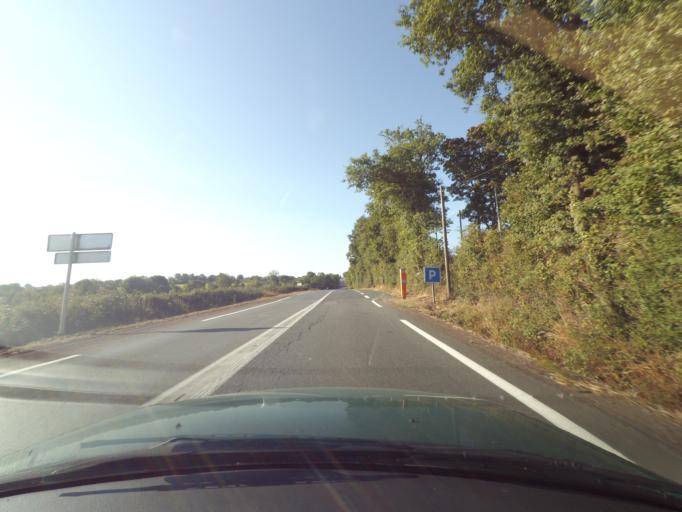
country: FR
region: Poitou-Charentes
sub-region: Departement des Deux-Sevres
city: Chiche
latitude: 46.7435
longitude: -0.3044
